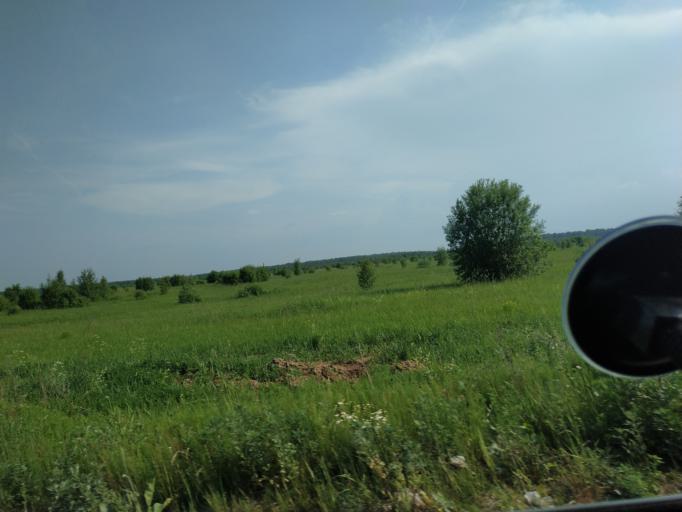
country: RU
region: Moskovskaya
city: Yakovlevskoye
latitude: 55.4307
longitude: 37.9384
